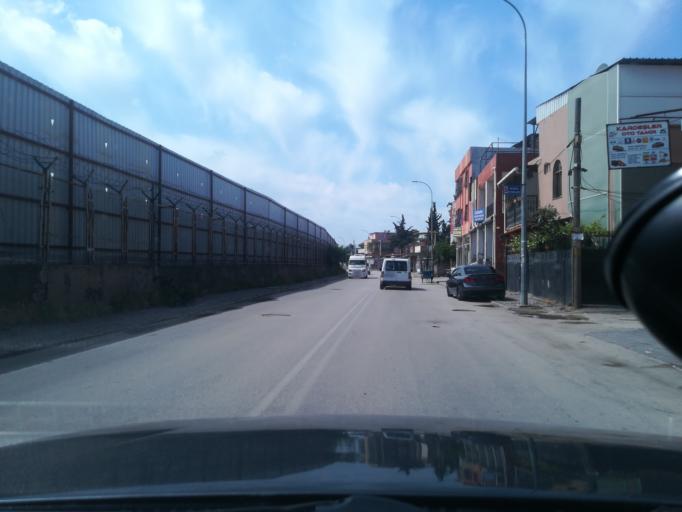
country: TR
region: Adana
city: Seyhan
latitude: 36.9908
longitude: 35.2873
